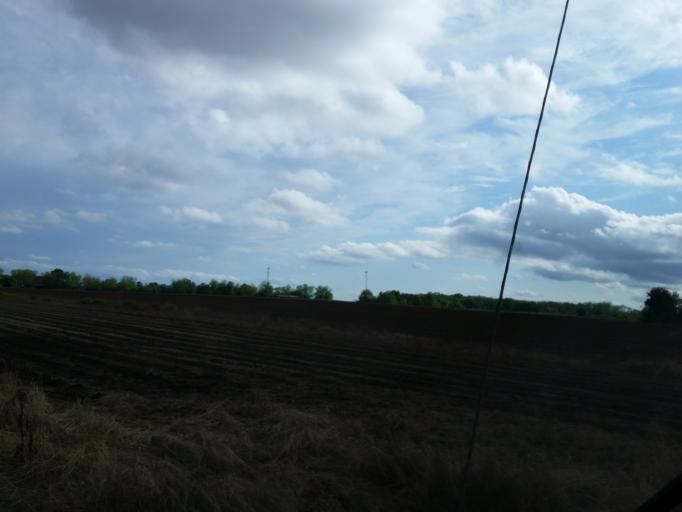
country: US
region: Georgia
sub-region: Dooly County
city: Unadilla
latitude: 32.1832
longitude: -83.7556
